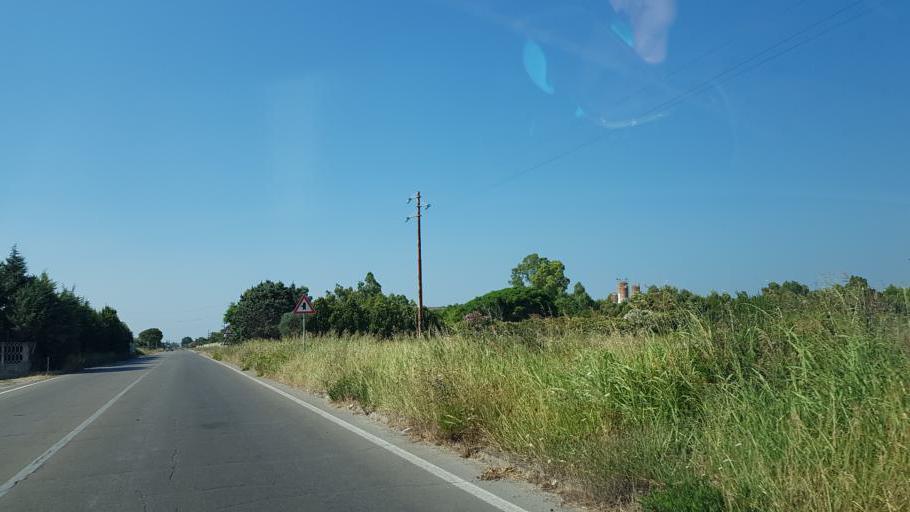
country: IT
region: Apulia
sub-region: Provincia di Lecce
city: Salice Salentino
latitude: 40.3697
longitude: 17.9670
